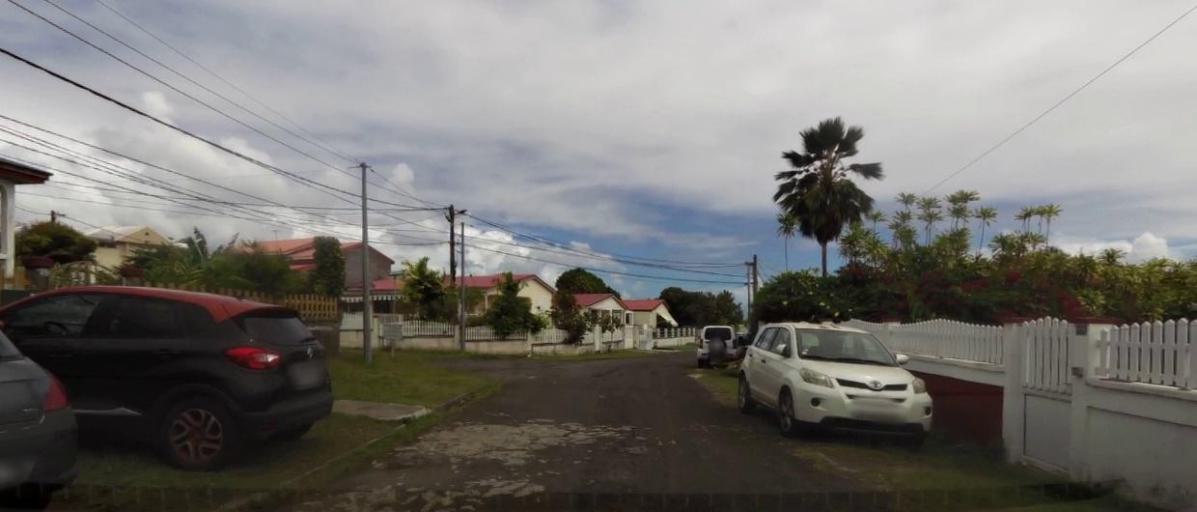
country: GP
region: Guadeloupe
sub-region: Guadeloupe
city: Petit-Bourg
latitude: 16.1977
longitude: -61.5916
